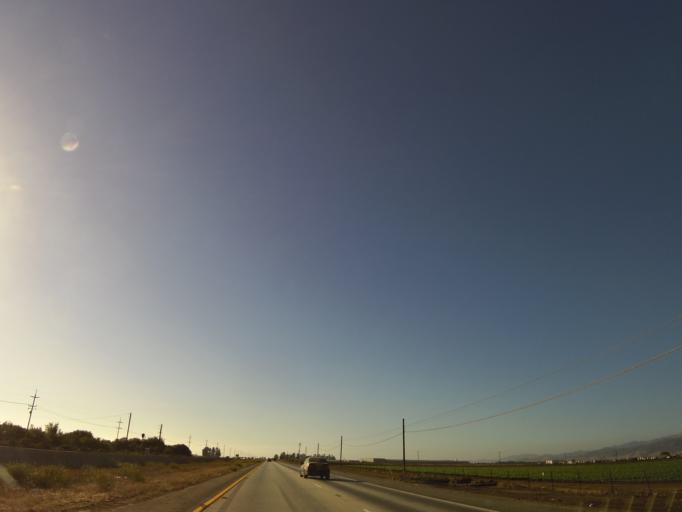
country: US
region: California
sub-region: Monterey County
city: Chualar
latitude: 36.5806
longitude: -121.5300
